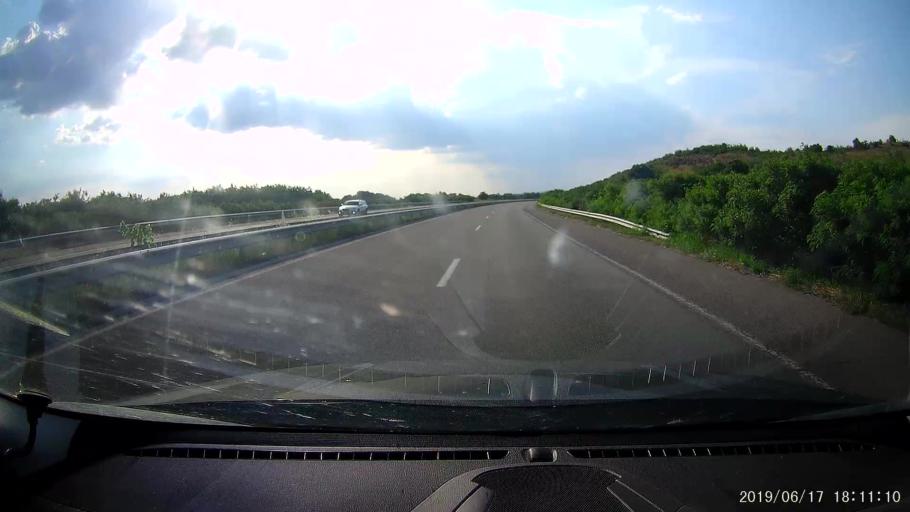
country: BG
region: Khaskovo
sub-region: Obshtina Lyubimets
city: Lyubimets
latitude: 41.8799
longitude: 26.0571
